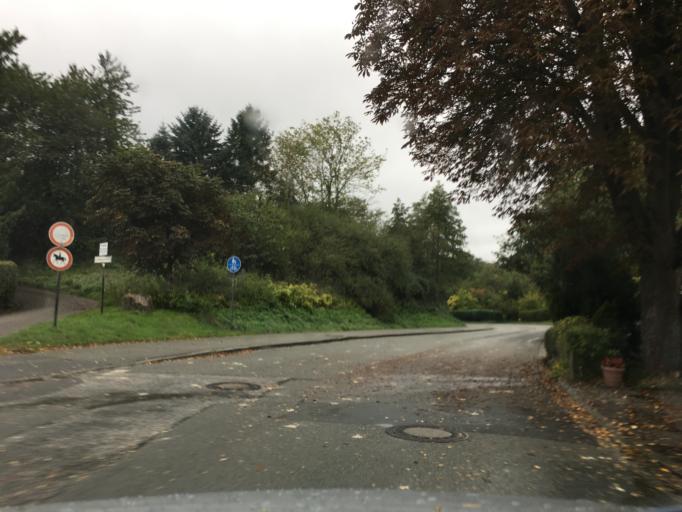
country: DE
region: Schleswig-Holstein
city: Quarnbek
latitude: 54.3444
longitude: 9.9890
